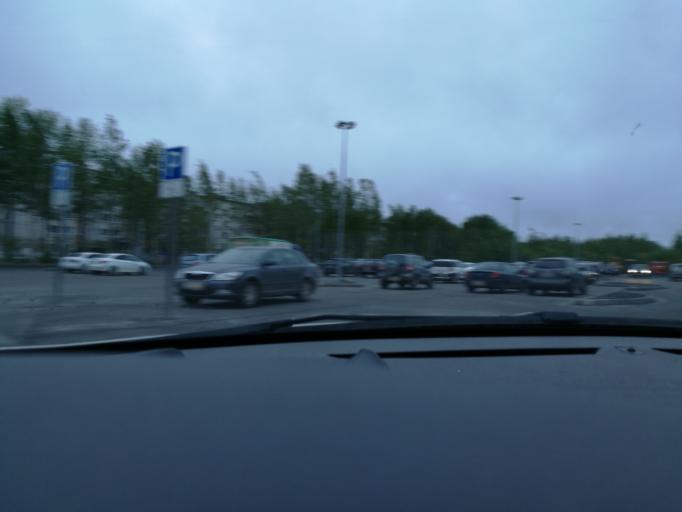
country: RU
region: Arkhangelskaya
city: Severodvinsk
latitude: 64.5566
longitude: 39.7764
